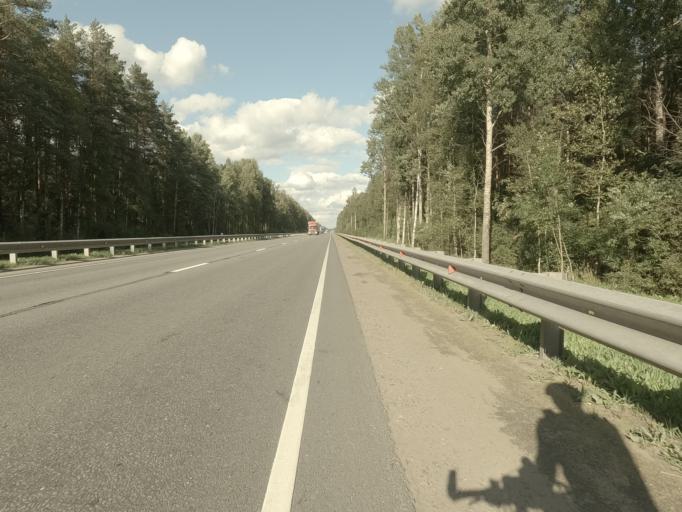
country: RU
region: Leningrad
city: Ul'yanovka
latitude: 59.6360
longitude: 30.8210
